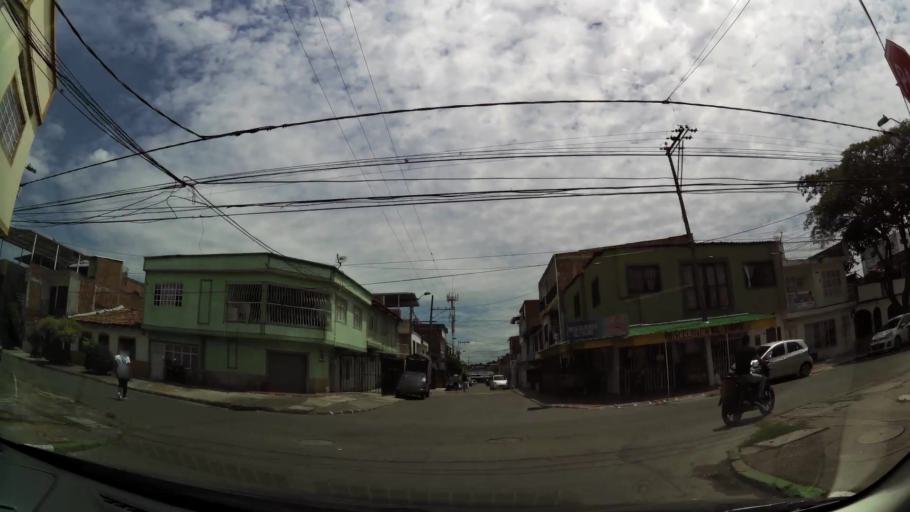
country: CO
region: Valle del Cauca
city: Cali
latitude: 3.4391
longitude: -76.5089
